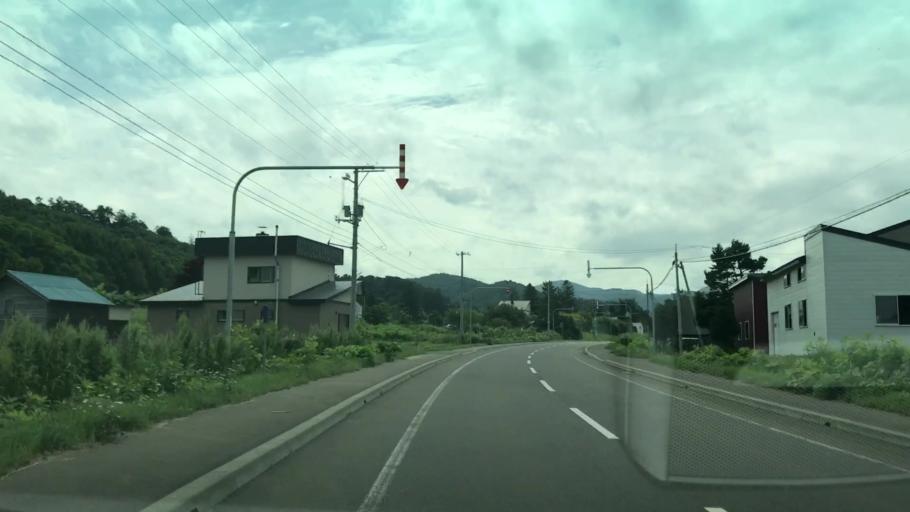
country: JP
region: Hokkaido
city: Yoichi
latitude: 43.1836
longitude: 140.8443
